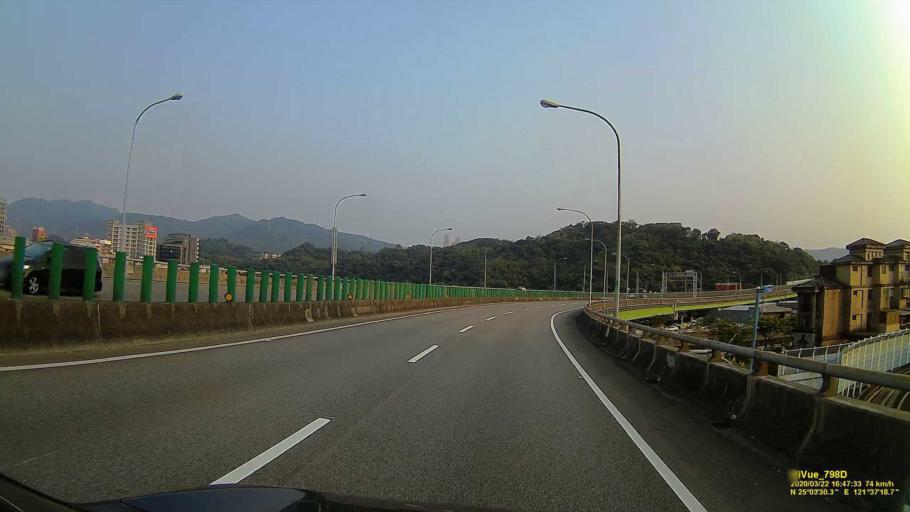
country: TW
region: Taipei
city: Taipei
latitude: 25.0580
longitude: 121.6221
